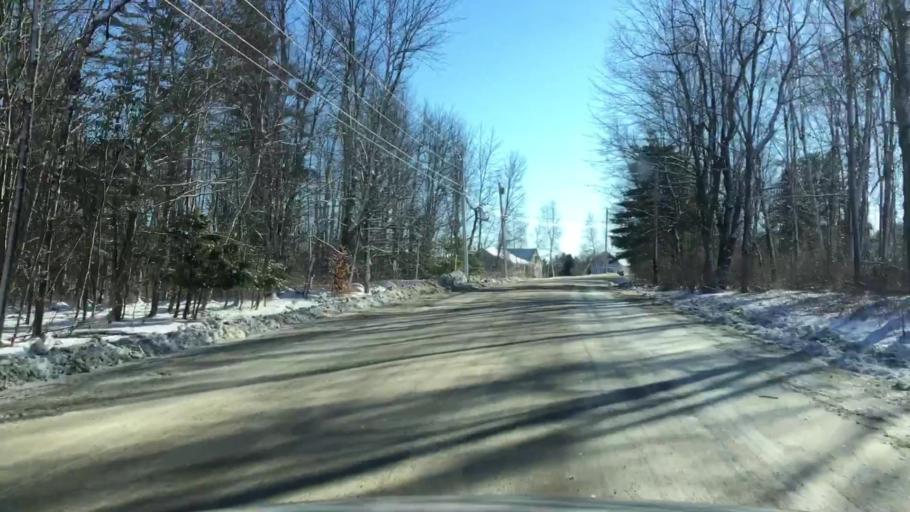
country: US
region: Maine
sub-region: Kennebec County
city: Winthrop
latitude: 44.3449
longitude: -69.9896
